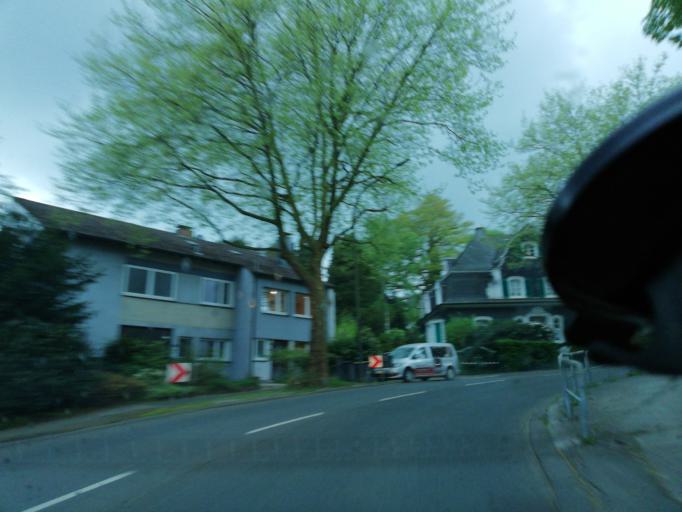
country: DE
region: North Rhine-Westphalia
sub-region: Regierungsbezirk Dusseldorf
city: Wuppertal
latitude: 51.2653
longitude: 7.2161
